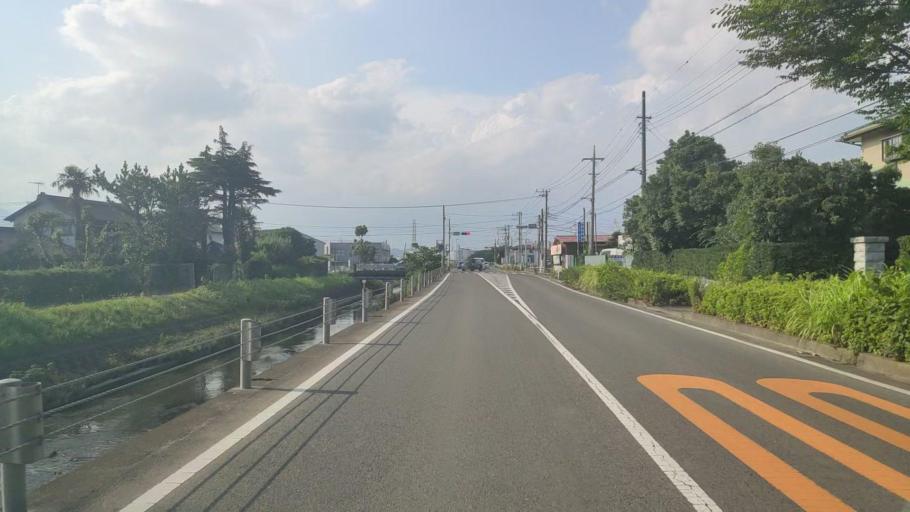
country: JP
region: Kanagawa
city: Isehara
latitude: 35.3897
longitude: 139.3384
